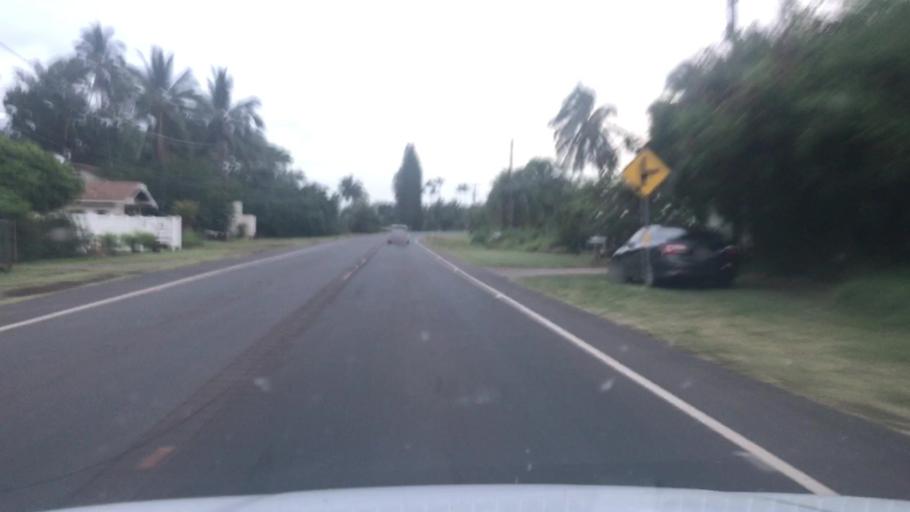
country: US
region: Hawaii
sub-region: Maui County
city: Kaunakakai
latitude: 21.0669
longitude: -156.9543
